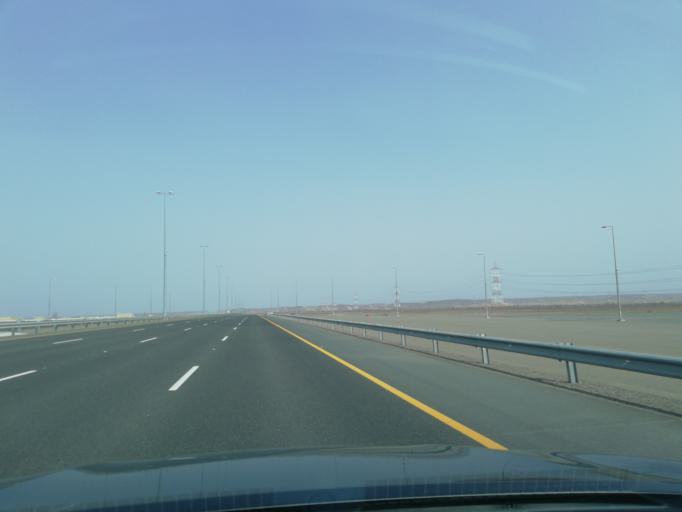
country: OM
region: Al Batinah
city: Al Sohar
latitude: 24.3170
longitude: 56.5779
